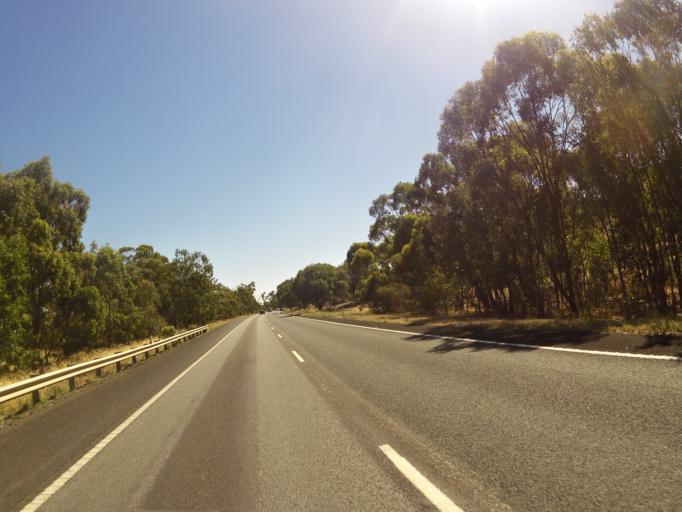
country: AU
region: Victoria
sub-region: Greater Shepparton
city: Shepparton
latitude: -36.8835
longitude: 145.2665
